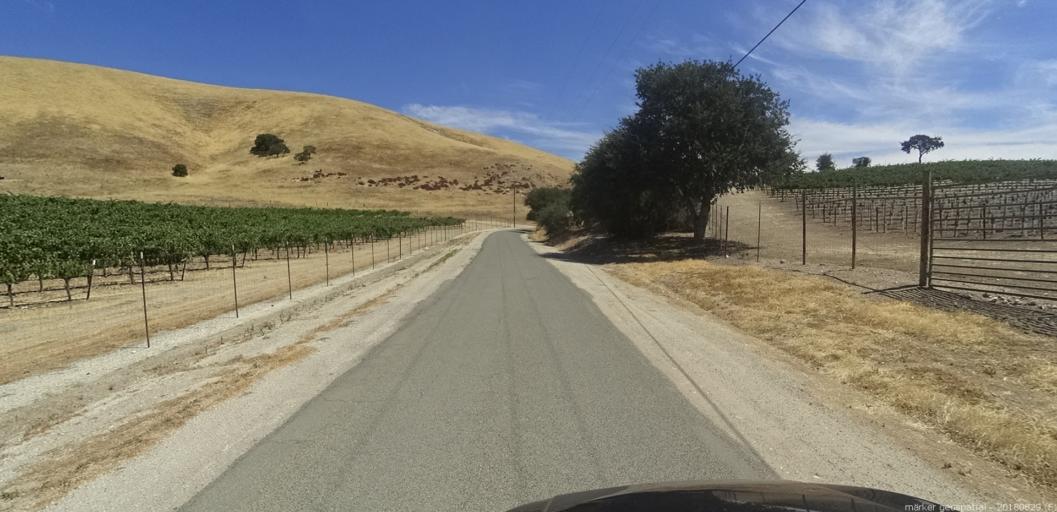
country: US
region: California
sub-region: San Luis Obispo County
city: Lake Nacimiento
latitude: 35.9083
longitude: -121.0169
